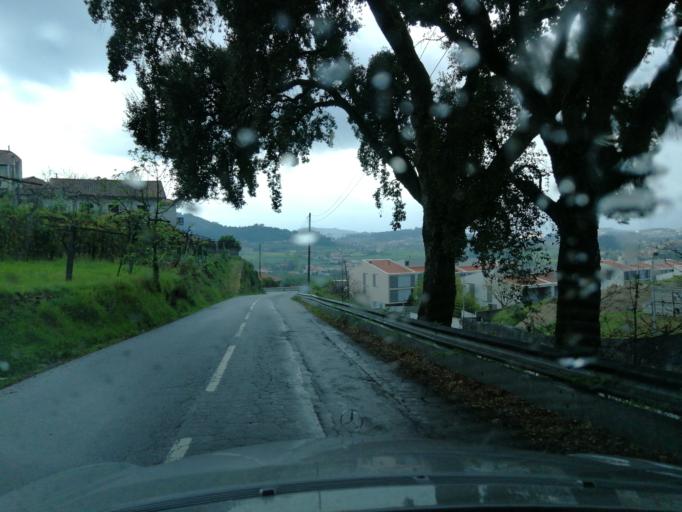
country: PT
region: Braga
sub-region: Vila Nova de Famalicao
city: Joane
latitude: 41.4796
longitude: -8.4249
